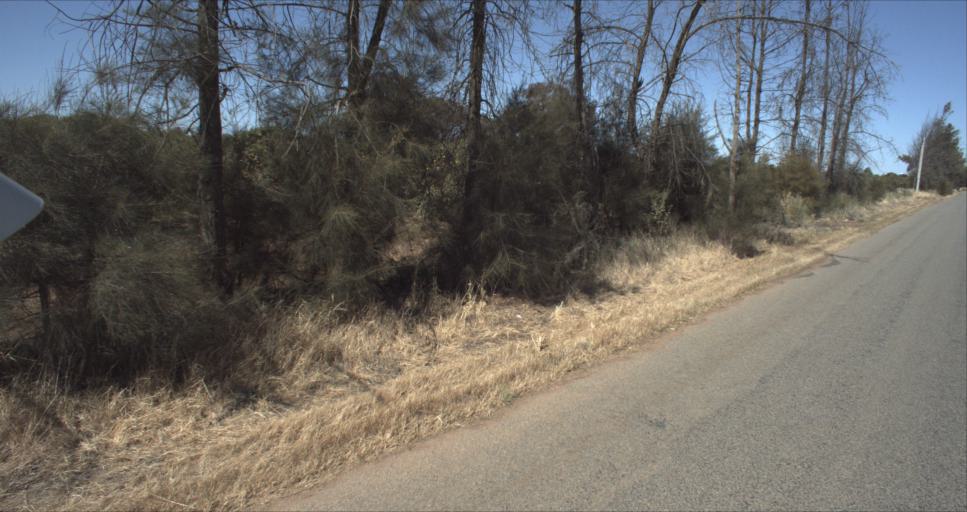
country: AU
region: New South Wales
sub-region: Leeton
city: Leeton
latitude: -34.5346
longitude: 146.3563
